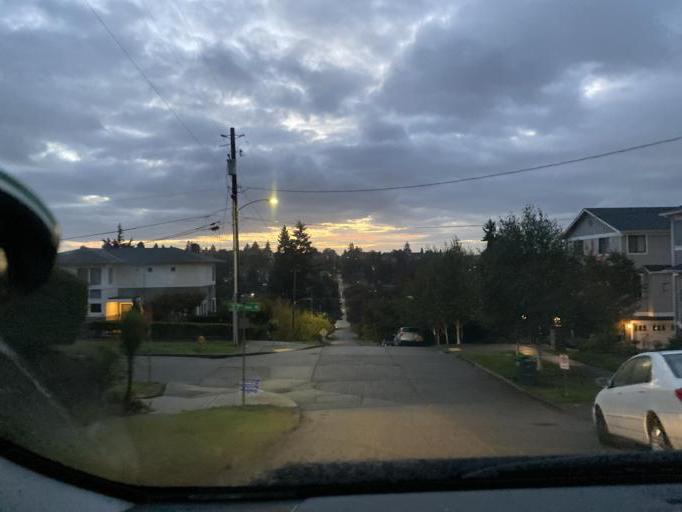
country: US
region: Washington
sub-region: King County
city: Seattle
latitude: 47.6468
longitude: -122.4051
